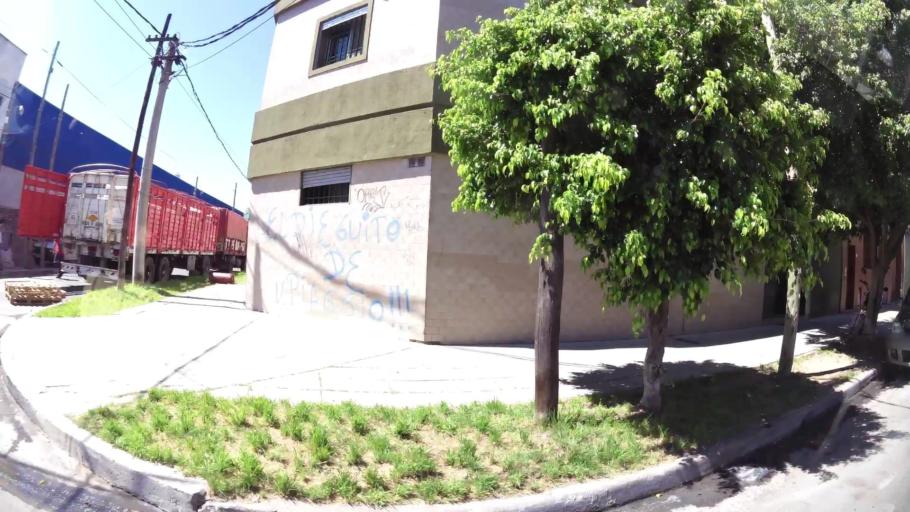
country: AR
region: Buenos Aires
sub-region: Partido de General San Martin
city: General San Martin
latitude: -34.5831
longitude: -58.5276
